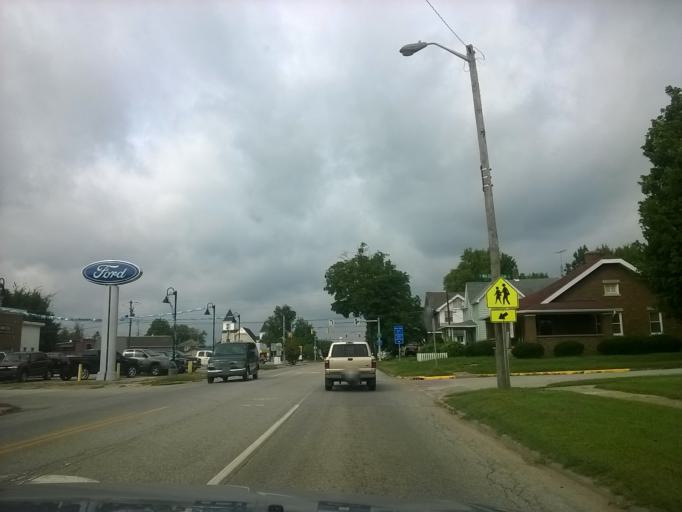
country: US
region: Indiana
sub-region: Owen County
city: Spencer
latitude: 39.2871
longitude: -86.7611
